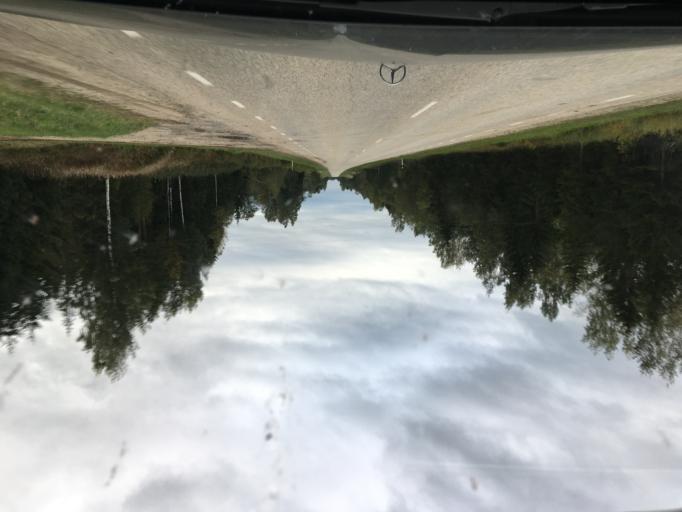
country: RU
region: Pskov
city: Pechory
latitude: 57.6342
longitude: 27.3311
